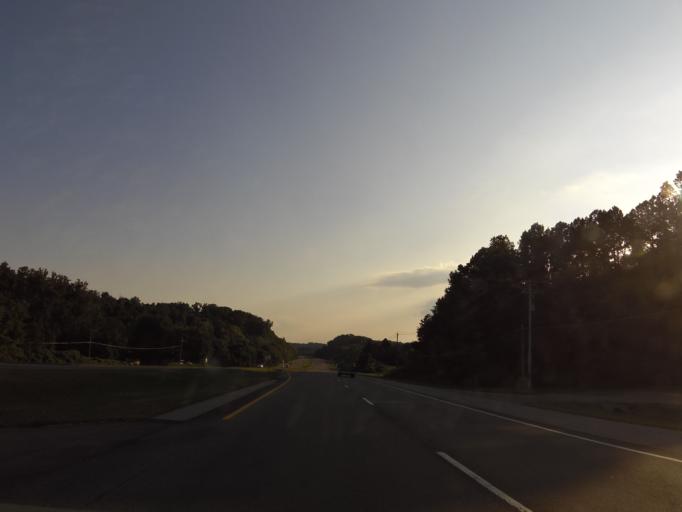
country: US
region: Tennessee
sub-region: Knox County
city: Mascot
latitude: 36.0902
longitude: -83.7571
